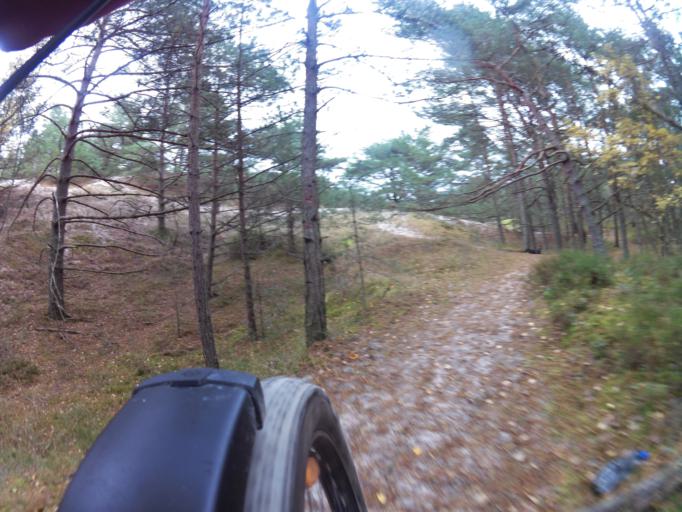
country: PL
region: Pomeranian Voivodeship
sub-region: Powiat leborski
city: Leba
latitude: 54.7702
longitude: 17.5921
